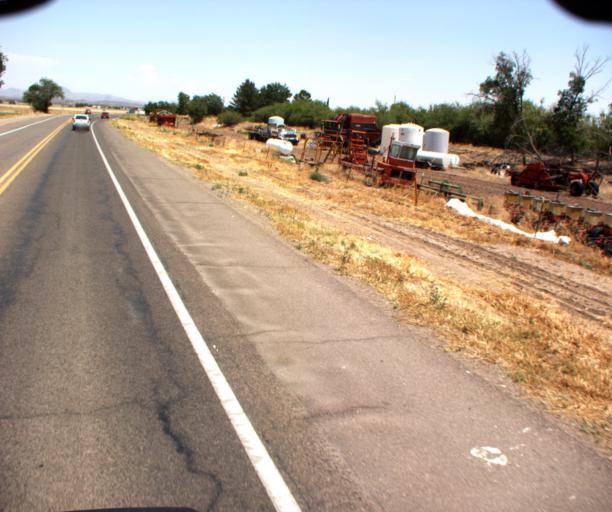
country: US
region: Arizona
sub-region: Graham County
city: Safford
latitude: 32.8166
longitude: -109.6336
